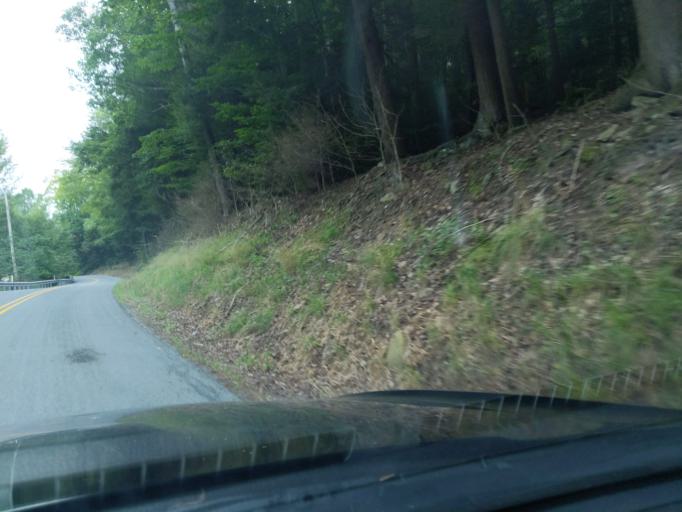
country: US
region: Pennsylvania
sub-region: Cambria County
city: Portage
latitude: 40.3389
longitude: -78.5821
